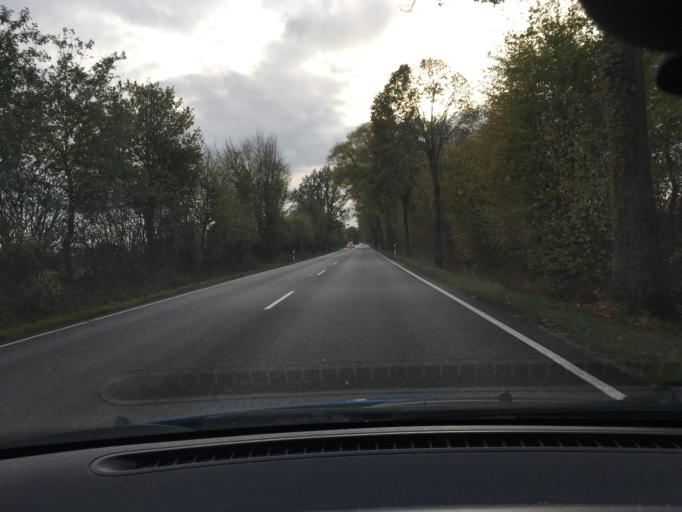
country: DE
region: Schleswig-Holstein
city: Kankelau
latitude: 53.5556
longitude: 10.5510
